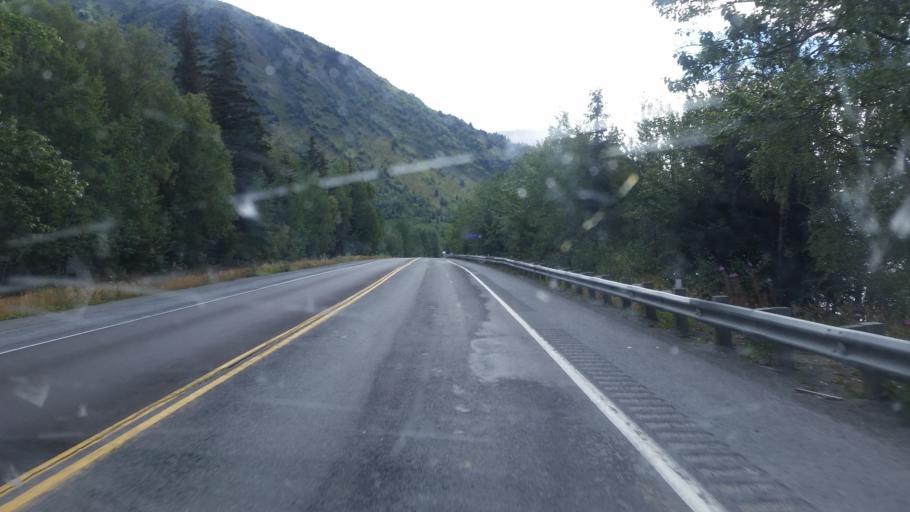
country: US
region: Alaska
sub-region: Anchorage Municipality
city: Elmendorf Air Force Base
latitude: 60.9864
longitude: -149.5104
